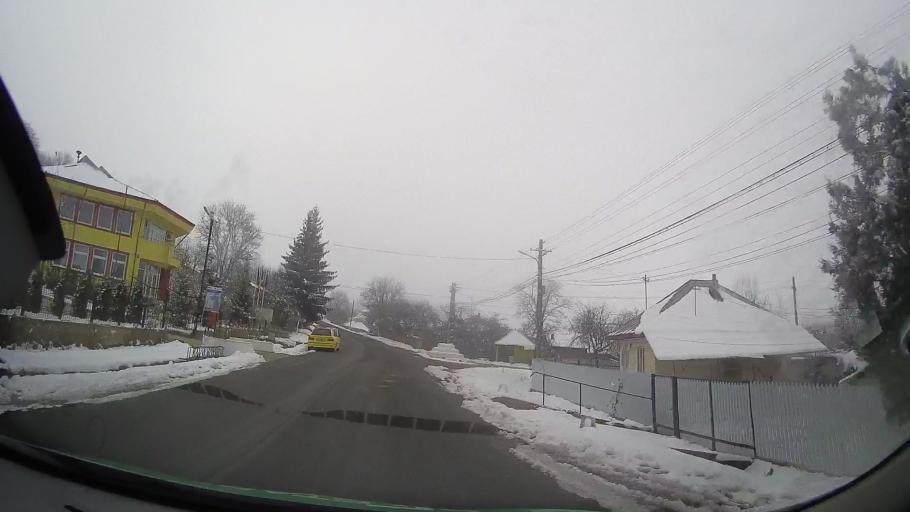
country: RO
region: Bacau
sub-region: Comuna Oncesti
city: Oncesti
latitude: 46.4717
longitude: 27.2557
